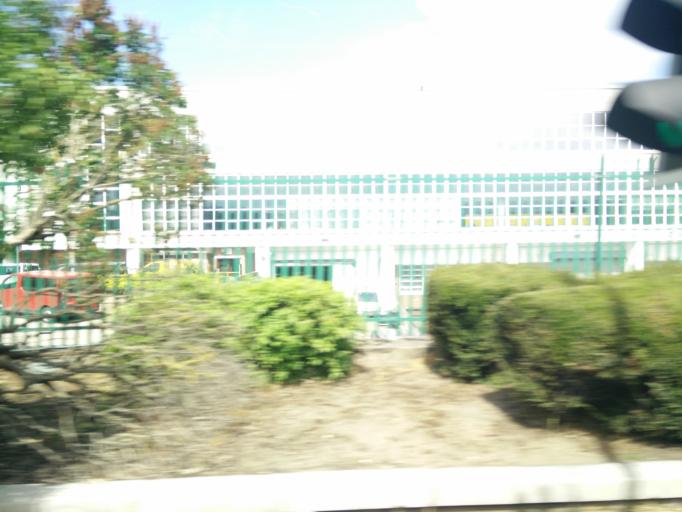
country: GB
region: England
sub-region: Luton
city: Luton
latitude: 51.8738
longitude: -0.3915
